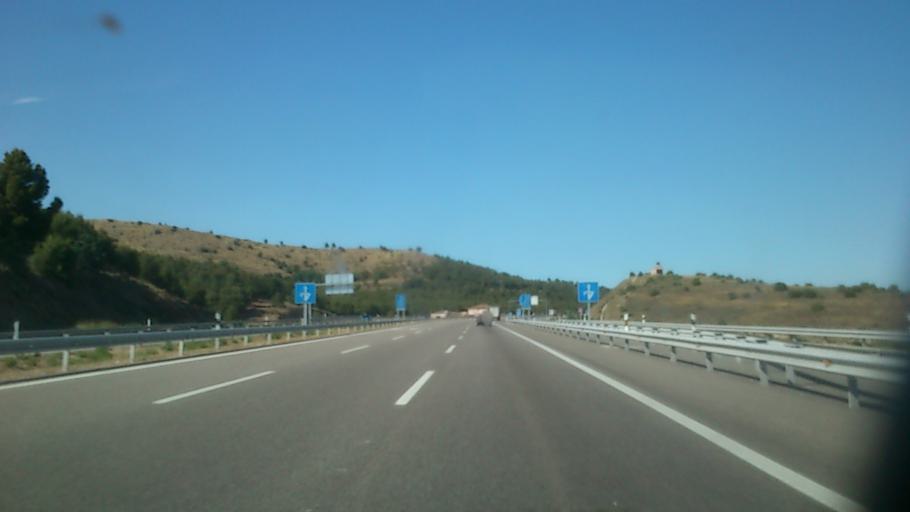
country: ES
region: Aragon
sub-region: Provincia de Zaragoza
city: Paracuellos de la Ribera
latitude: 41.3856
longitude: -1.5679
